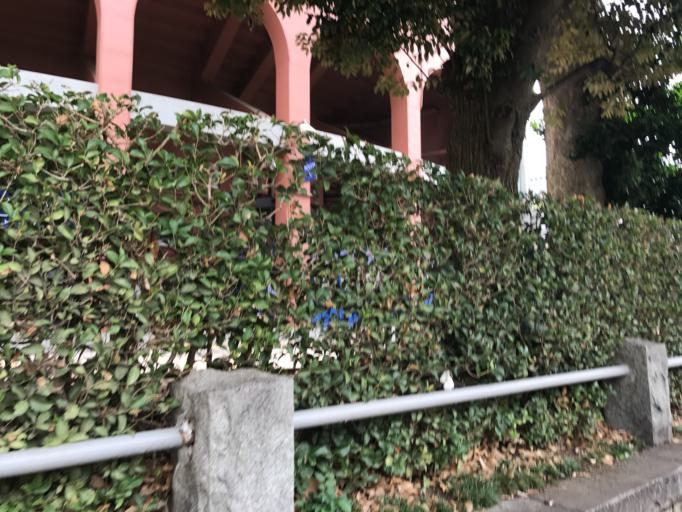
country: JP
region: Tokyo
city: Tokyo
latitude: 35.6738
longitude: 139.7159
